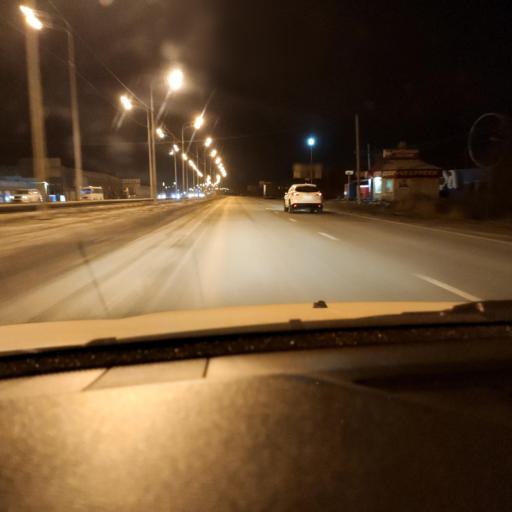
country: RU
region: Samara
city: Smyshlyayevka
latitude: 53.2619
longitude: 50.3813
